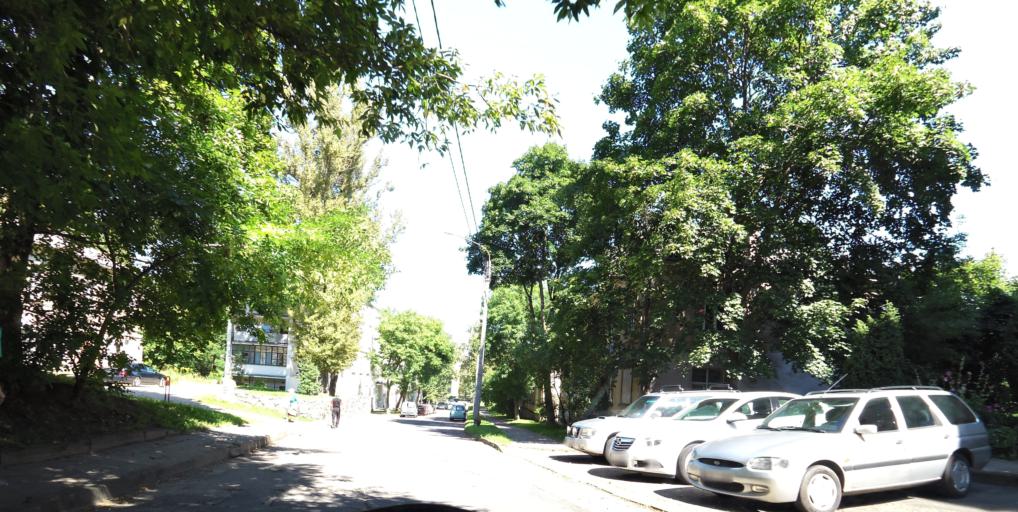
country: LT
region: Vilnius County
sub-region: Vilnius
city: Vilnius
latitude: 54.6671
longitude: 25.2892
